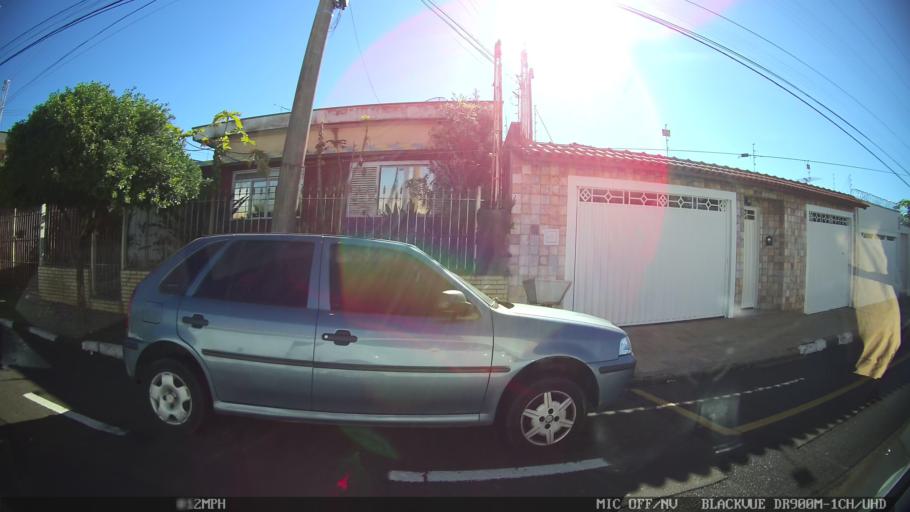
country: BR
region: Sao Paulo
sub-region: Franca
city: Franca
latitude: -20.5288
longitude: -47.4104
